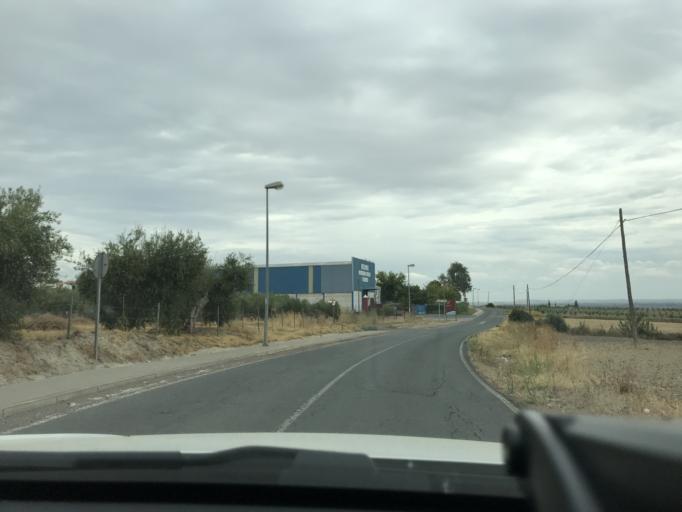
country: ES
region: Andalusia
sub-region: Provincia de Sevilla
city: Villanueva del Rio y Minas
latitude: 37.6461
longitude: -5.7088
